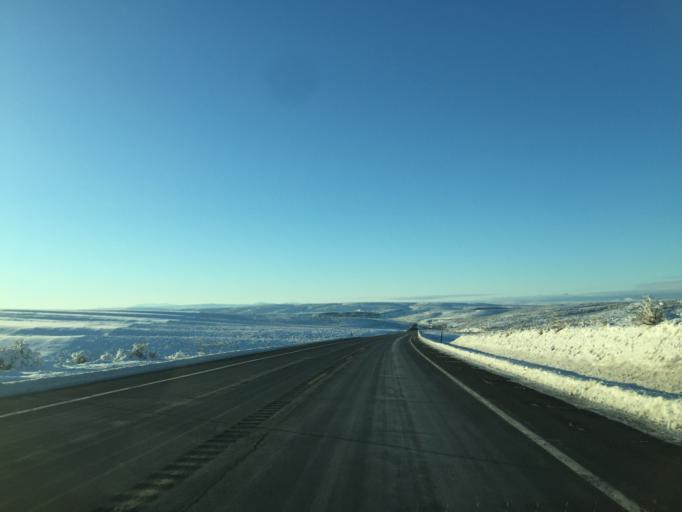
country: US
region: Washington
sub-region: Grant County
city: Soap Lake
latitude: 47.5998
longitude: -119.6106
